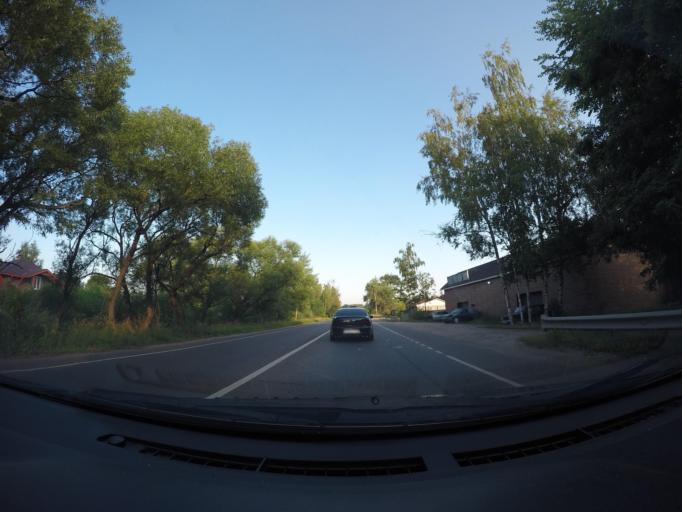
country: RU
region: Moskovskaya
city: Il'inskiy
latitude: 55.6441
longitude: 38.1504
